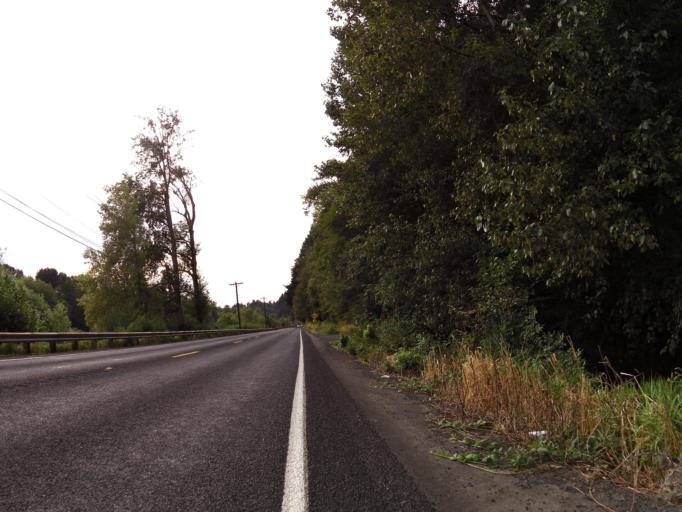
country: US
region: Washington
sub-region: Cowlitz County
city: West Longview
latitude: 46.1887
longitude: -123.1038
